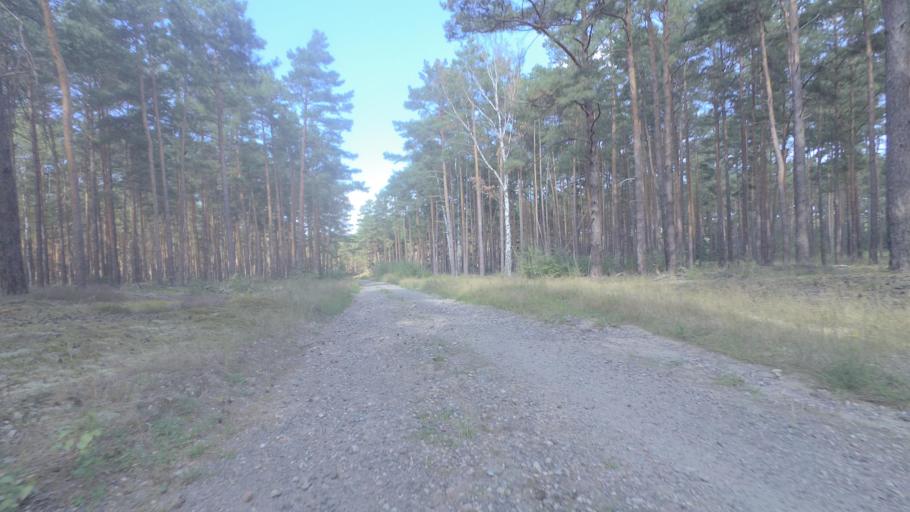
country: DE
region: Brandenburg
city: Munchehofe
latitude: 52.1820
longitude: 13.8720
